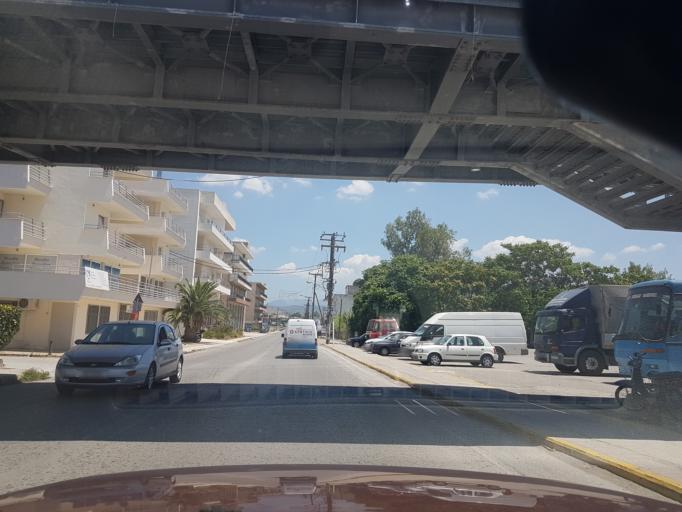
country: GR
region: Central Greece
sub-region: Nomos Evvoias
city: Chalkida
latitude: 38.4696
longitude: 23.6120
